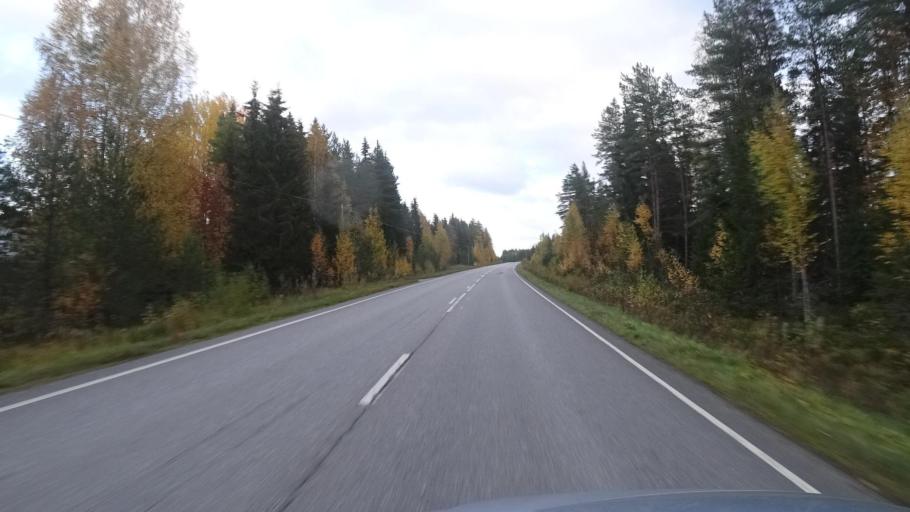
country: FI
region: Varsinais-Suomi
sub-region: Loimaa
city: Ylaene
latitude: 60.9958
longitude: 22.5007
